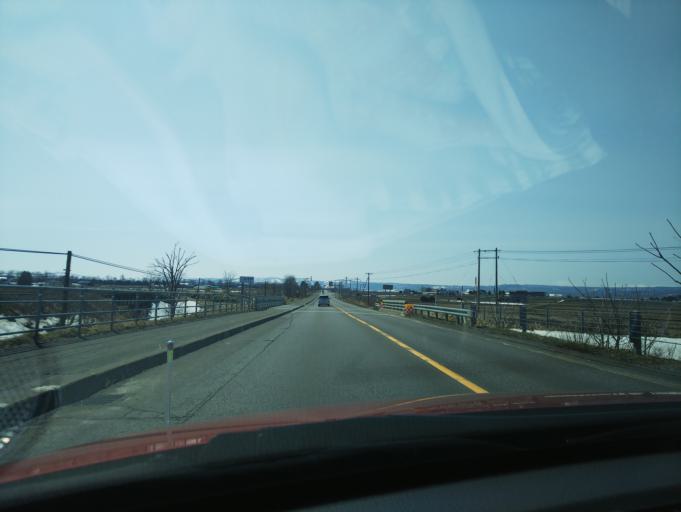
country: JP
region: Hokkaido
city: Nayoro
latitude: 44.3129
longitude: 142.4536
